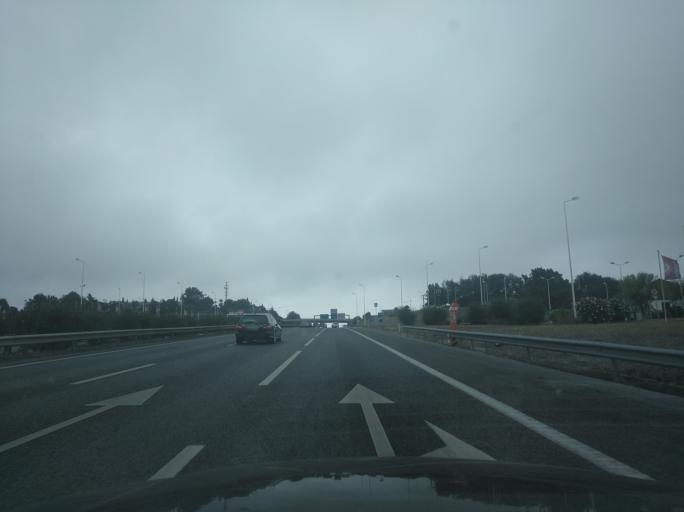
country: PT
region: Lisbon
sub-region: Oeiras
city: Terrugem
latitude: 38.7145
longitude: -9.2847
